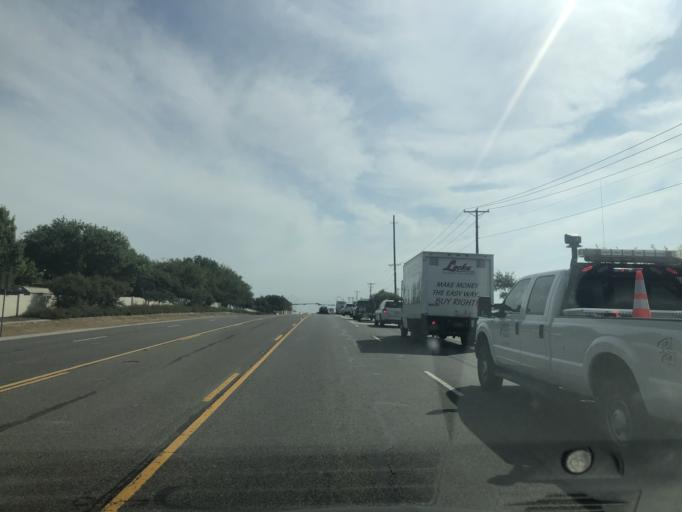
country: US
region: Texas
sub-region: Tarrant County
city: Benbrook
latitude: 32.6669
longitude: -97.4775
